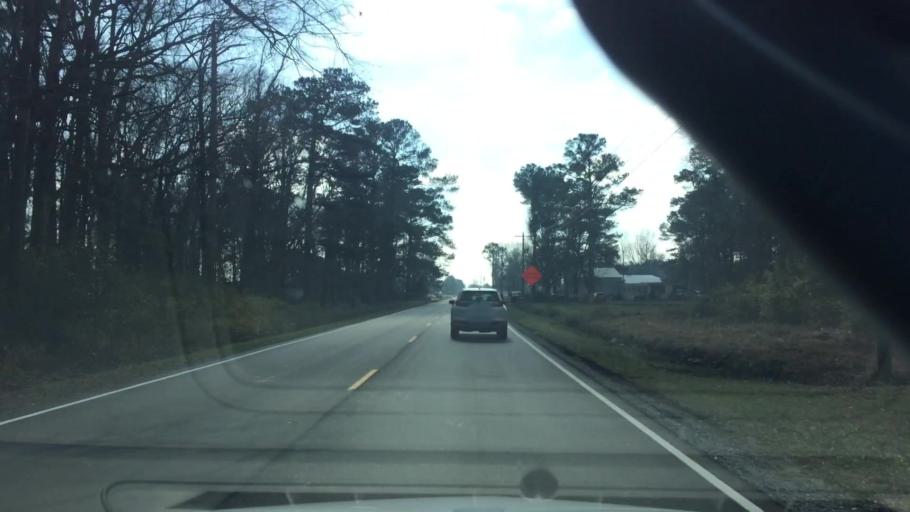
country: US
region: North Carolina
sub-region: Duplin County
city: Beulaville
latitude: 34.9630
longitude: -77.7641
